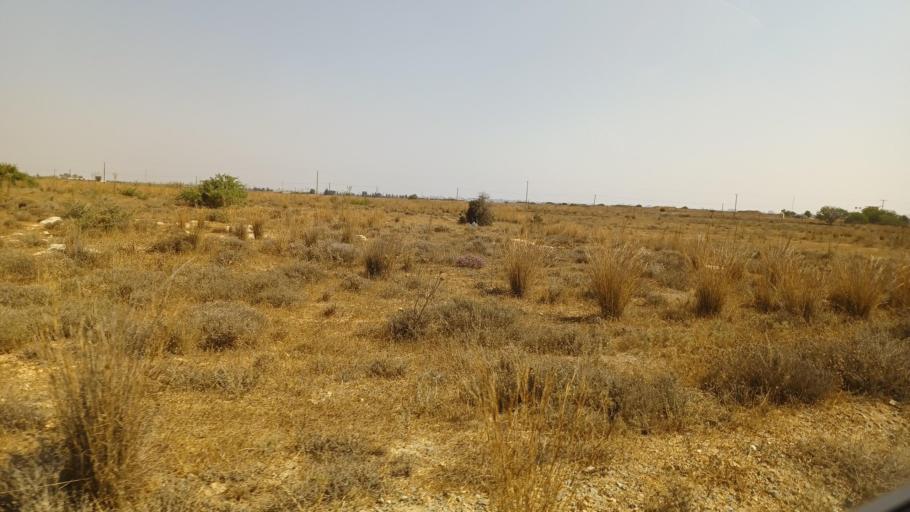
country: CY
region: Ammochostos
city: Frenaros
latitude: 35.0674
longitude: 33.9222
